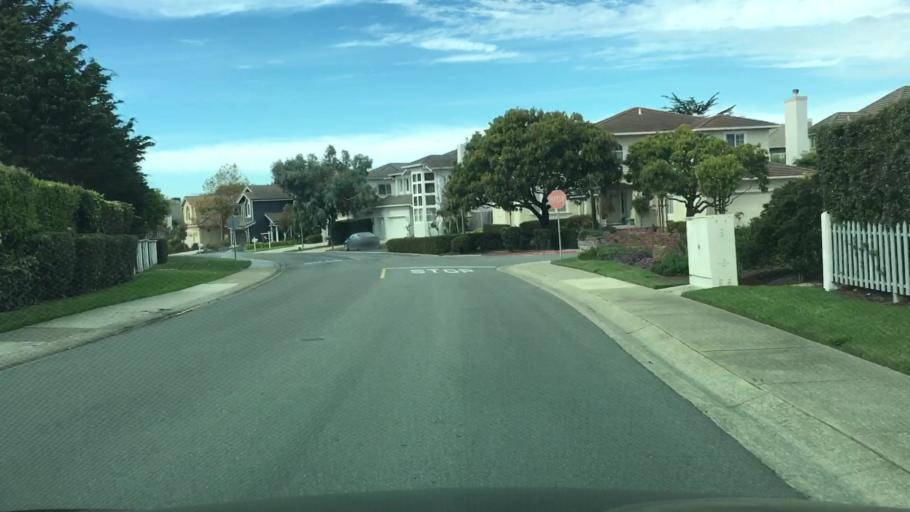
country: US
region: California
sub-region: San Mateo County
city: Half Moon Bay
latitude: 37.4363
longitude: -122.4311
